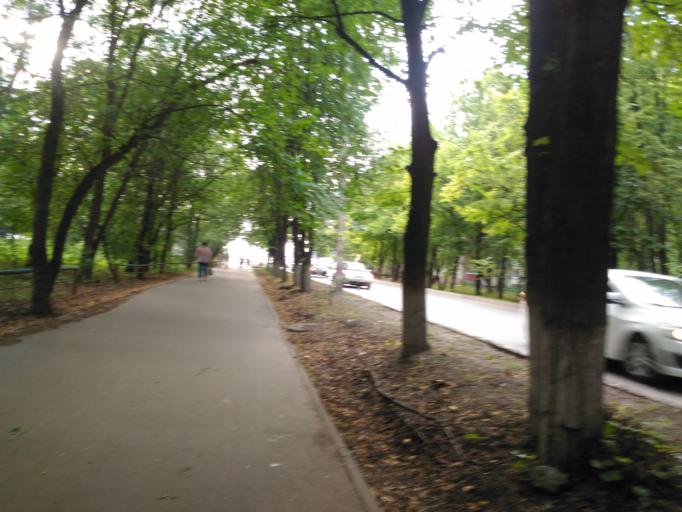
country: RU
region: Ulyanovsk
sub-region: Ulyanovskiy Rayon
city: Ulyanovsk
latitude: 54.2846
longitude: 48.2862
